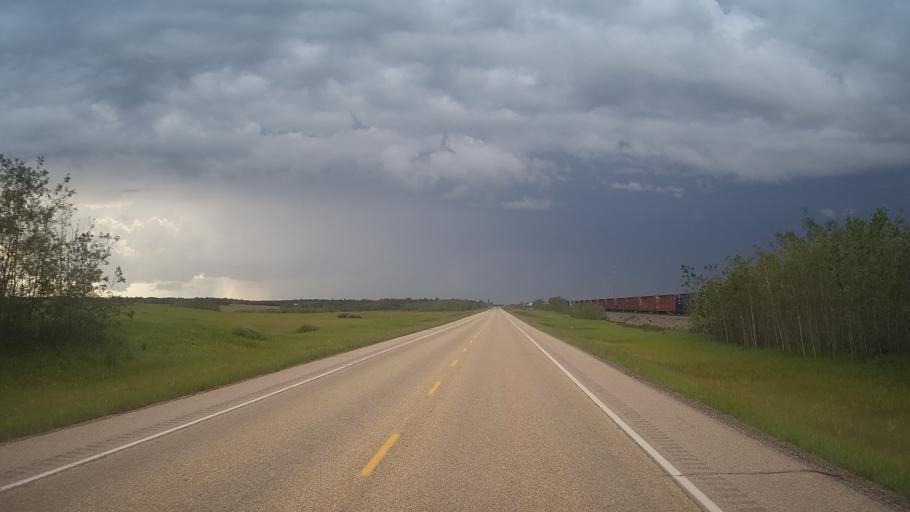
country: CA
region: Alberta
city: Tofield
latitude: 53.2748
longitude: -112.3861
